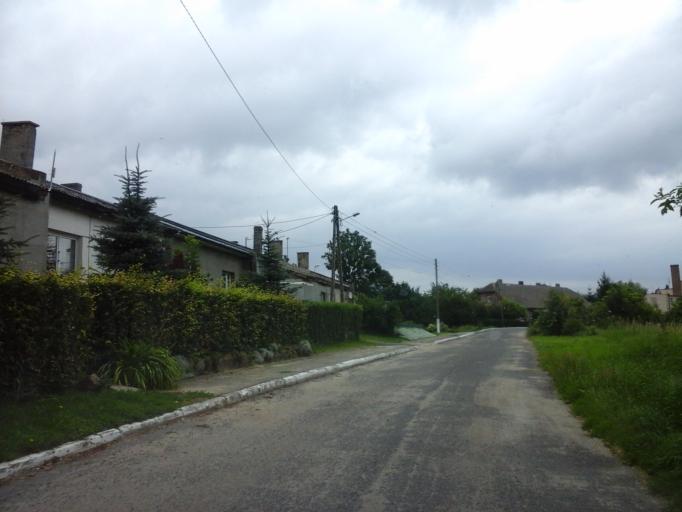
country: PL
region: West Pomeranian Voivodeship
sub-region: Powiat choszczenski
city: Krzecin
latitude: 53.0341
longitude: 15.4515
